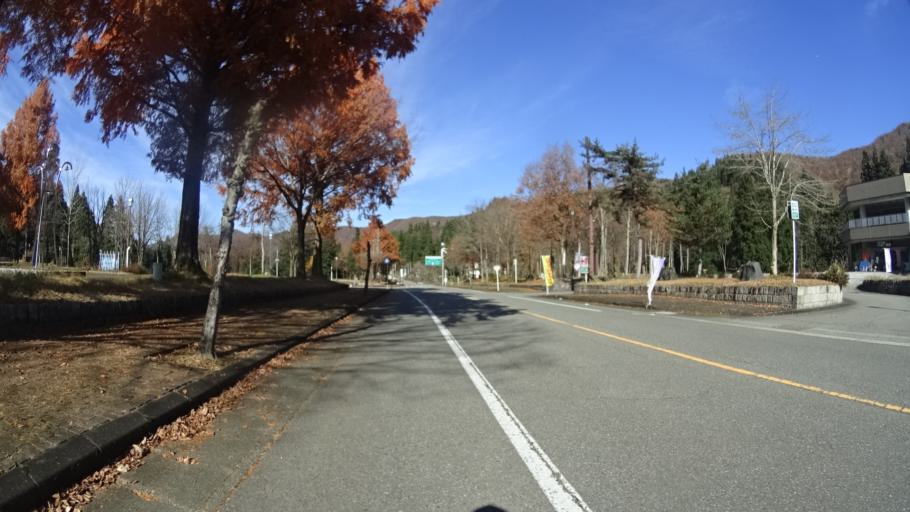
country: JP
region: Niigata
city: Muikamachi
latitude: 37.1970
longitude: 139.0771
